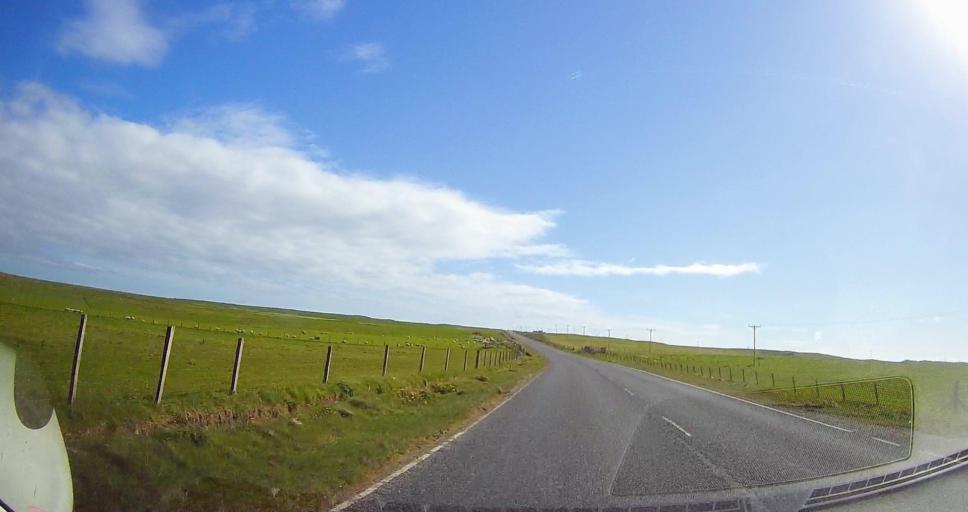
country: GB
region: Scotland
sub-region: Shetland Islands
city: Sandwick
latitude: 59.9081
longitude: -1.3018
